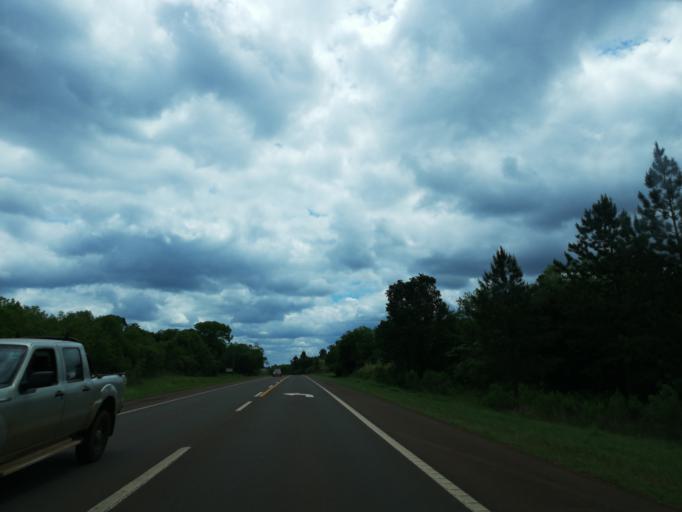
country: AR
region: Misiones
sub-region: Departamento de Leandro N. Alem
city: Leandro N. Alem
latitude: -27.6434
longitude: -55.3793
